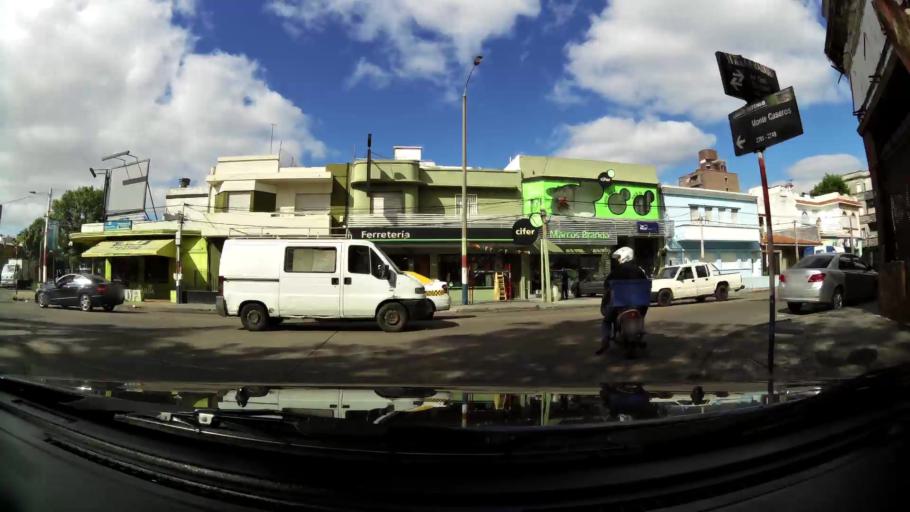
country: UY
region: Montevideo
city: Montevideo
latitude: -34.8860
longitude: -56.1640
